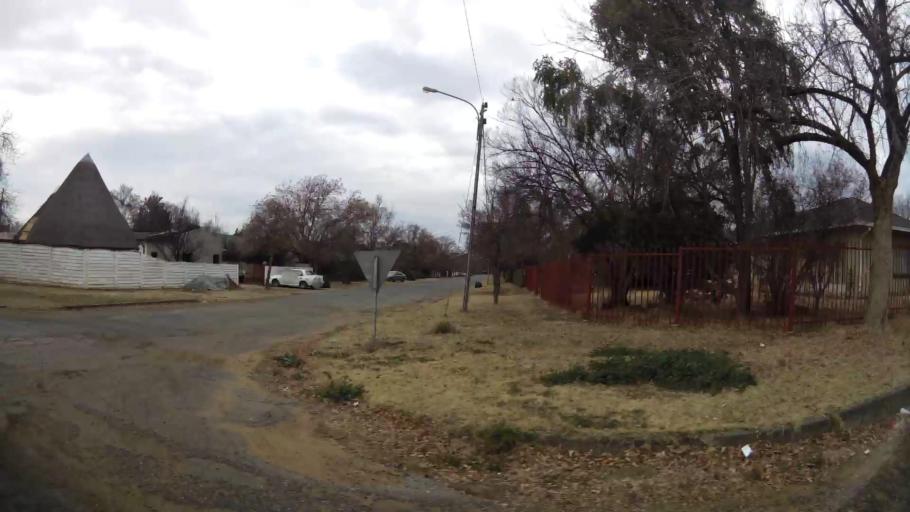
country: ZA
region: Orange Free State
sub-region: Fezile Dabi District Municipality
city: Kroonstad
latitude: -27.6846
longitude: 27.2353
